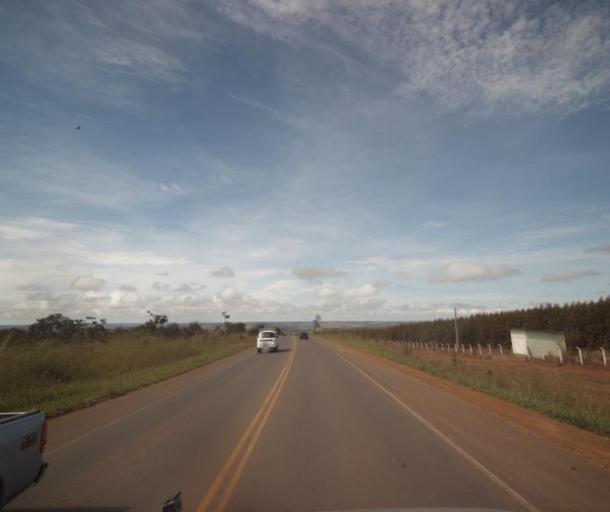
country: BR
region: Goias
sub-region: Abadiania
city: Abadiania
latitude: -16.0648
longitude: -48.8545
